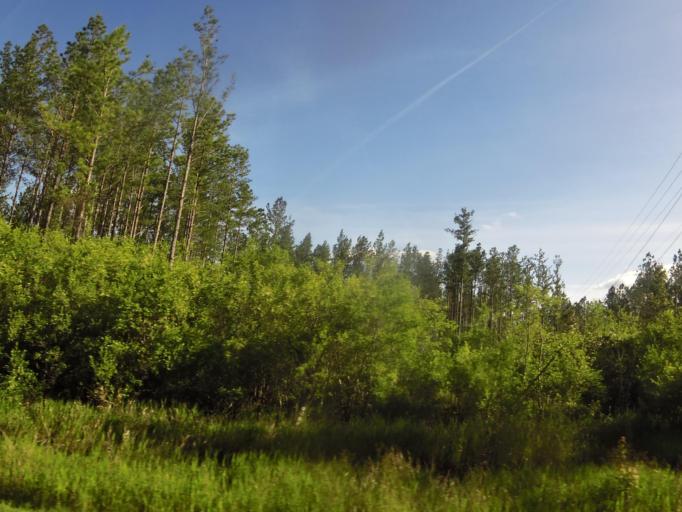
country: US
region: Florida
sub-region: Nassau County
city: Nassau Village-Ratliff
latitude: 30.4585
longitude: -81.8300
